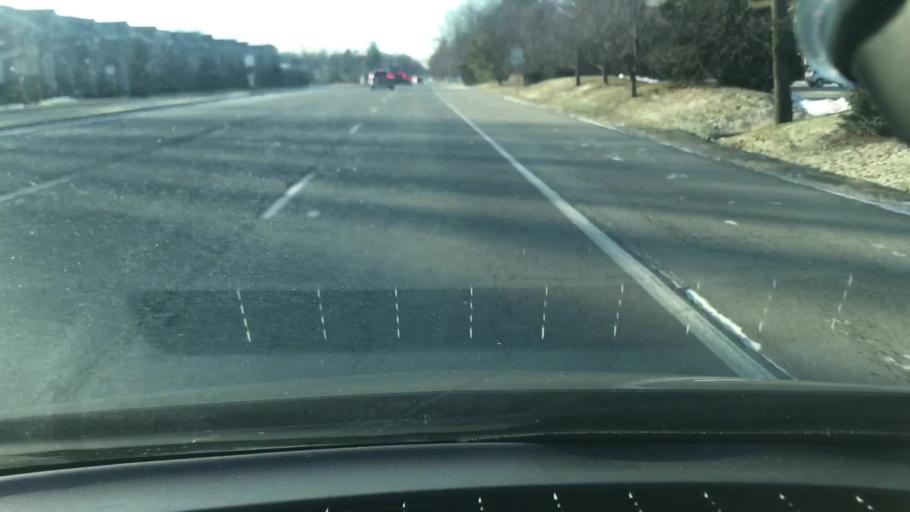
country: US
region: Indiana
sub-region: Marion County
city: Meridian Hills
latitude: 39.9150
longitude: -86.1582
